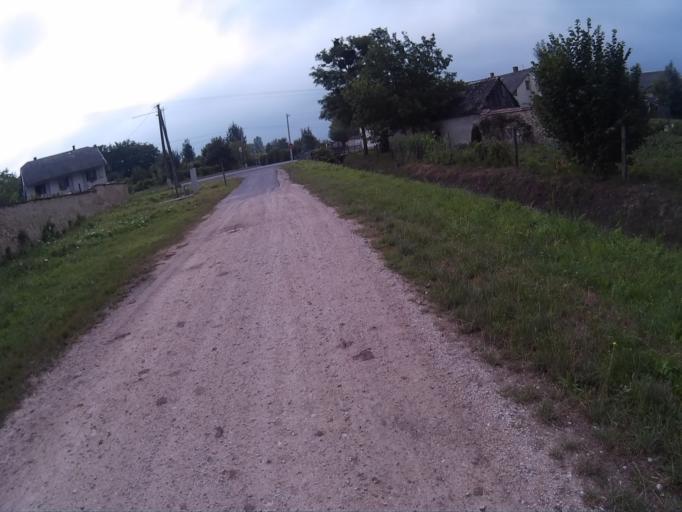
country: HU
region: Veszprem
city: Papa
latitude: 47.2845
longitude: 17.5187
